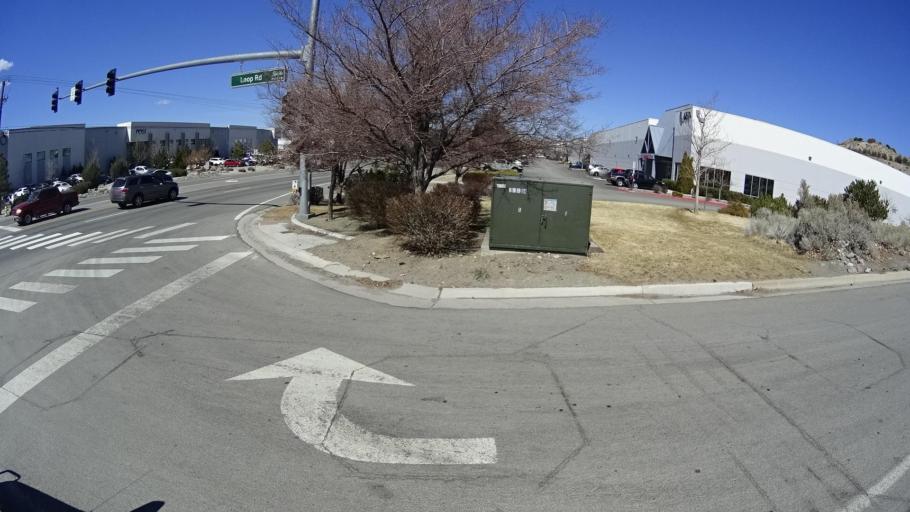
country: US
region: Nevada
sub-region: Washoe County
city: Sparks
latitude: 39.5372
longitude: -119.7034
